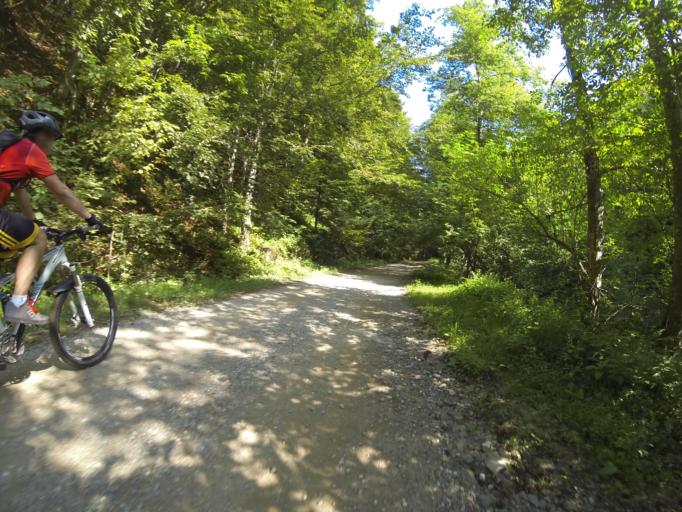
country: RO
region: Valcea
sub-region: Comuna Costesti
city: Bistrita
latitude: 45.2282
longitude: 24.0027
